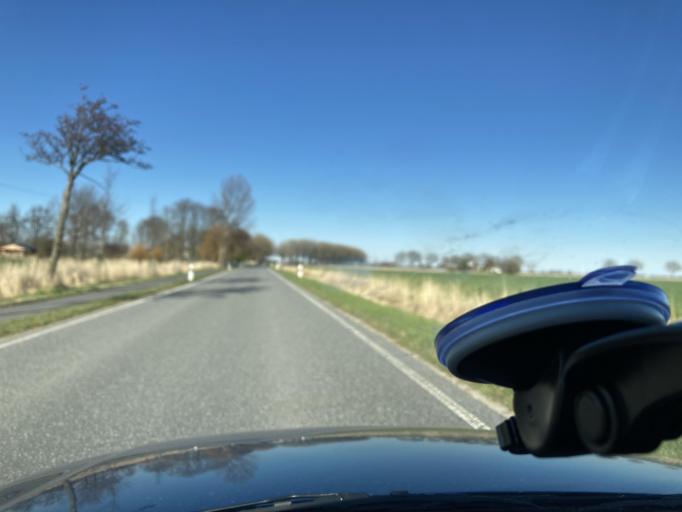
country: DE
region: Schleswig-Holstein
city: Wesselburen
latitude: 54.2232
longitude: 8.9468
